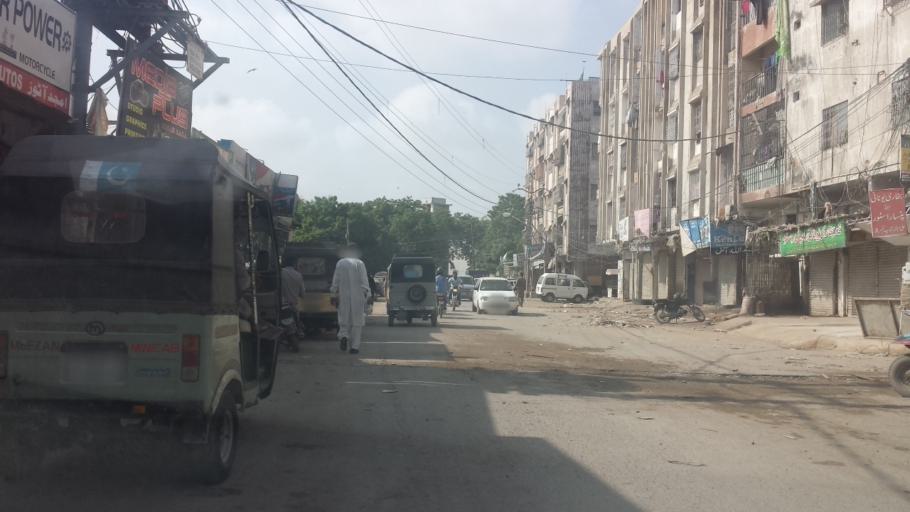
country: PK
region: Sindh
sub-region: Karachi District
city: Karachi
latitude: 24.9455
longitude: 67.0771
